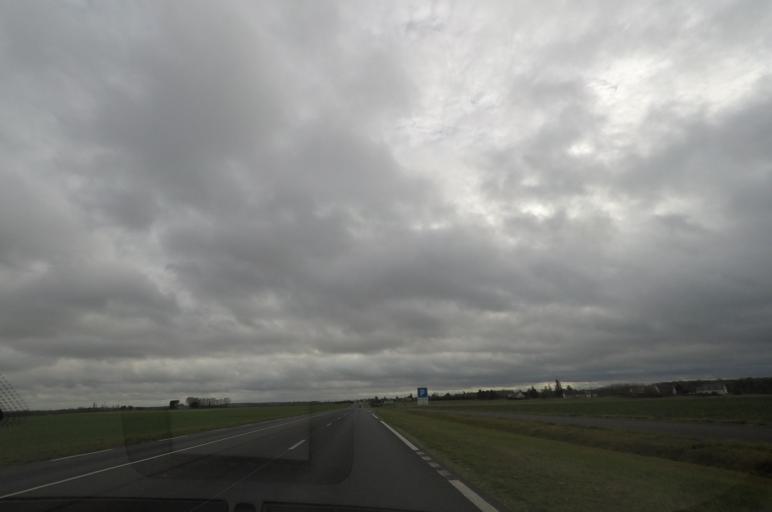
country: FR
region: Centre
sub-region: Departement du Loir-et-Cher
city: Saint-Sulpice-de-Pommeray
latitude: 47.6639
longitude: 1.2544
